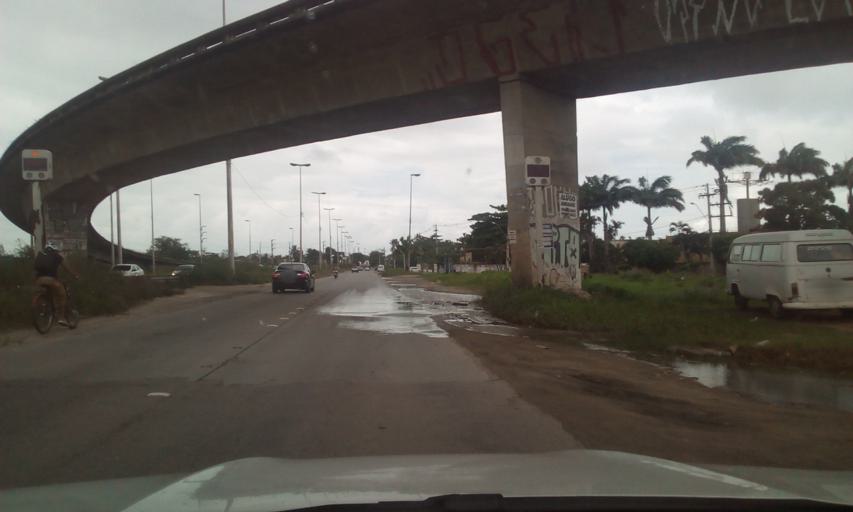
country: BR
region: Pernambuco
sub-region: Recife
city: Recife
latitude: -8.0745
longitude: -34.9370
